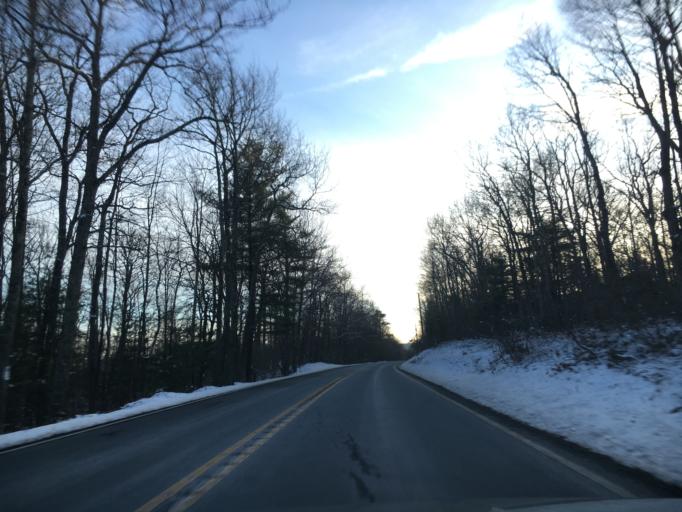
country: US
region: Pennsylvania
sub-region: Pike County
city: Hemlock Farms
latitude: 41.3513
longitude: -75.1298
